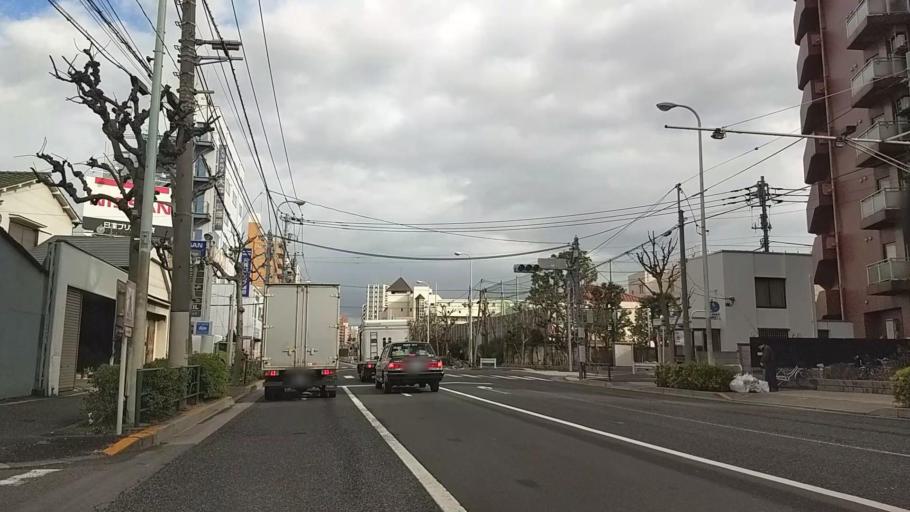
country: JP
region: Kanagawa
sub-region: Kawasaki-shi
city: Kawasaki
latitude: 35.5680
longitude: 139.7356
